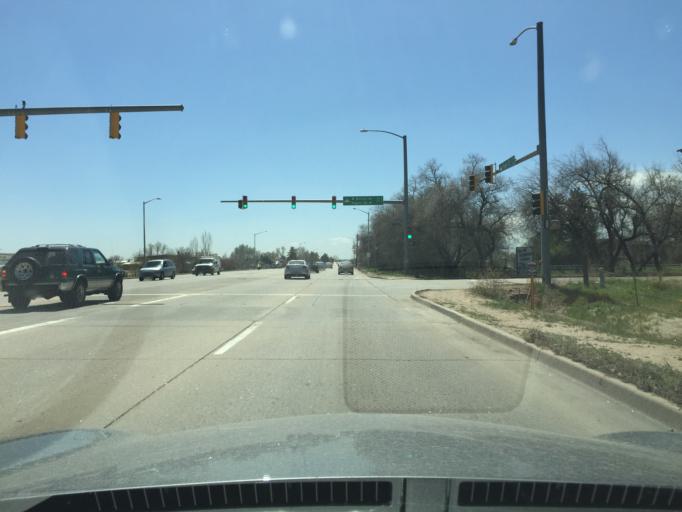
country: US
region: Colorado
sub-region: Boulder County
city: Longmont
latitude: 40.1601
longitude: -105.1308
